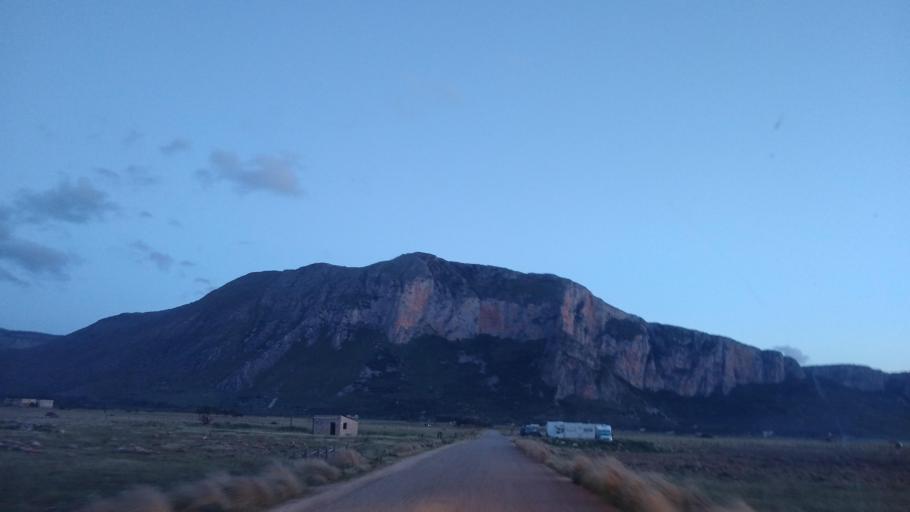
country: IT
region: Sicily
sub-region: Trapani
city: Castelluzzo
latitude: 38.1174
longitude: 12.7211
